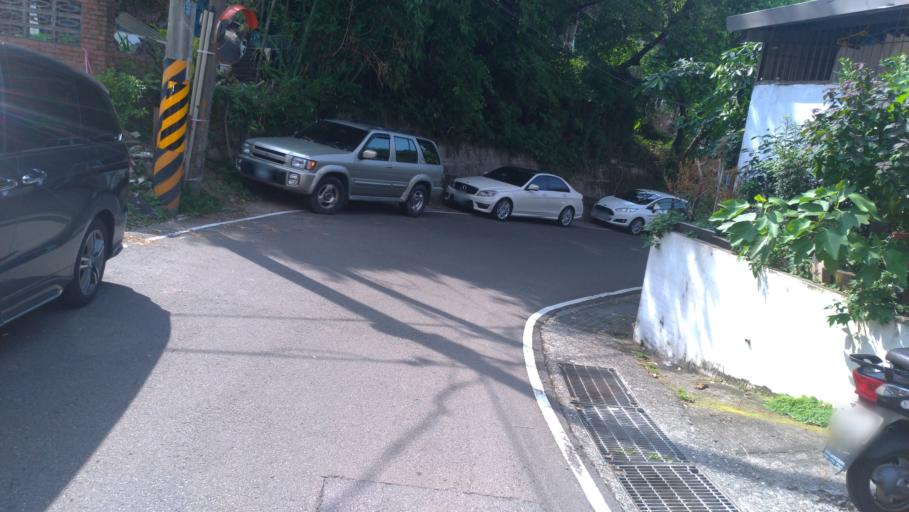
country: TW
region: Taiwan
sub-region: Keelung
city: Keelung
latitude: 25.1188
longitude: 121.8185
